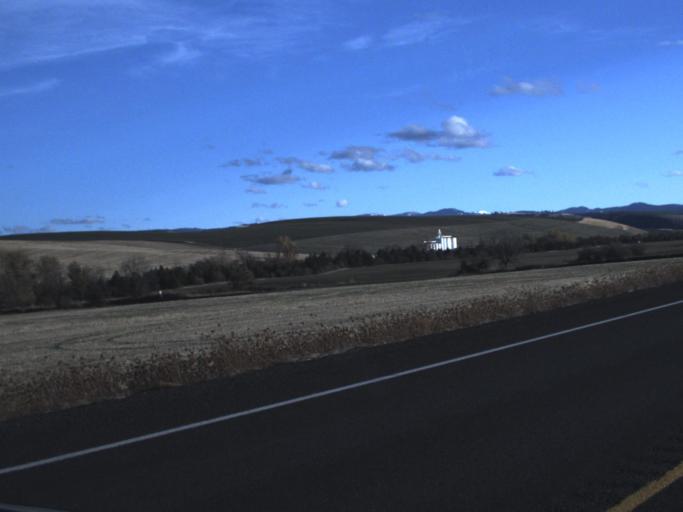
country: US
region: Washington
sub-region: Walla Walla County
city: Waitsburg
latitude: 46.2309
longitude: -118.1378
